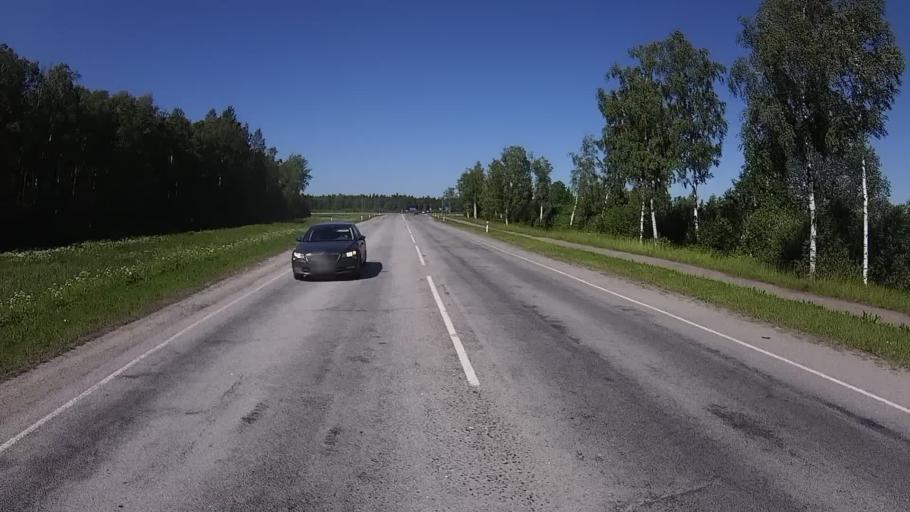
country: EE
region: Ida-Virumaa
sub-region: Kohtla-Jaerve linn
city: Kohtla-Jarve
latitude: 59.4179
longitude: 27.2749
